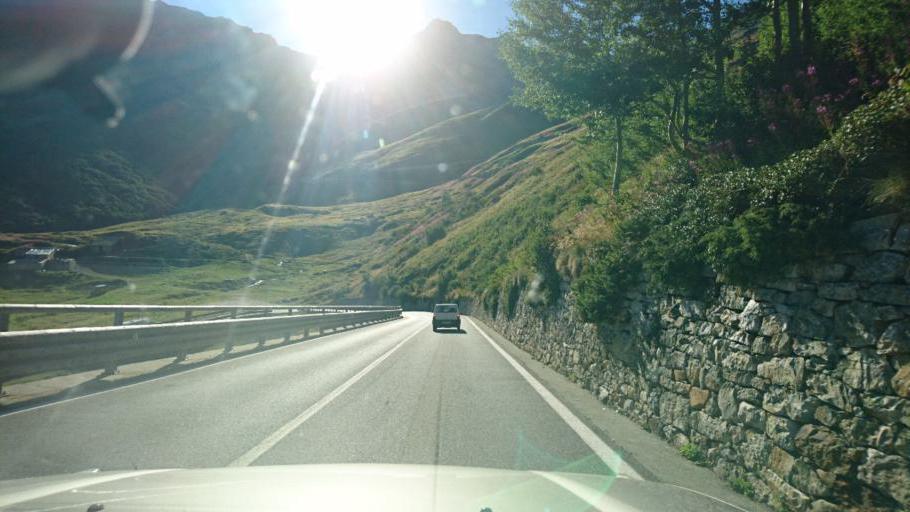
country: IT
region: Aosta Valley
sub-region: Valle d'Aosta
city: San Leonardo
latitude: 45.8566
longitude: 7.1523
